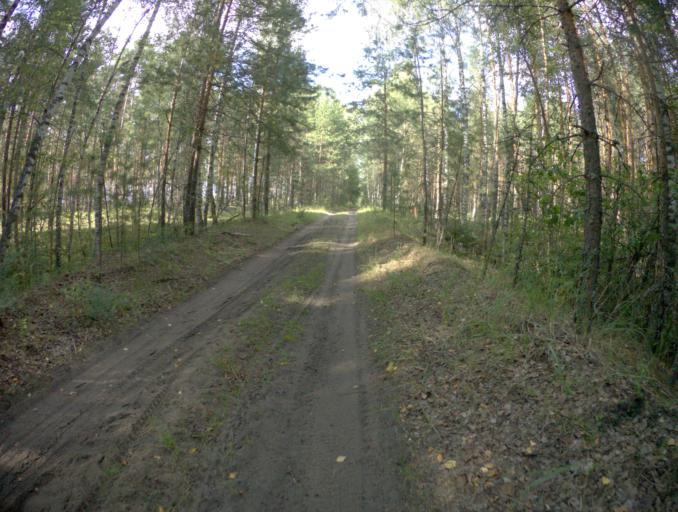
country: RU
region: Vladimir
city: Sobinka
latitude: 55.9527
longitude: 40.0595
